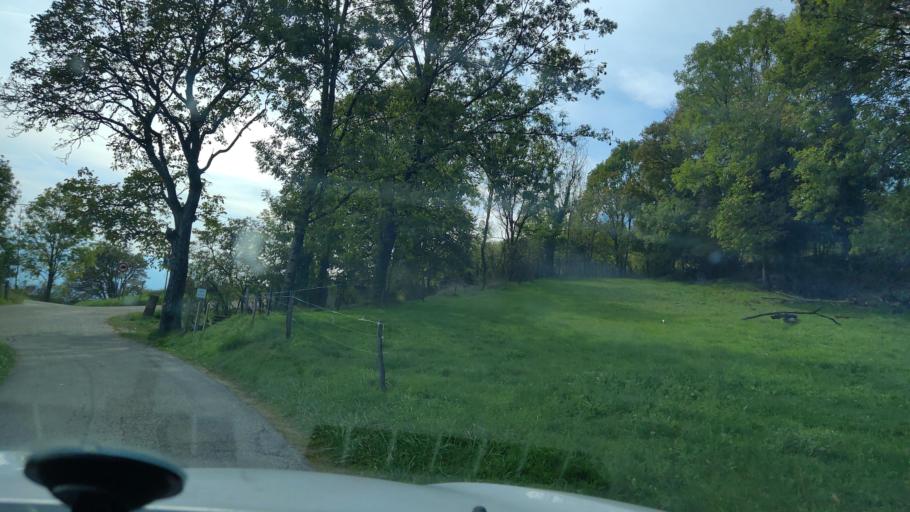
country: FR
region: Rhone-Alpes
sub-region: Departement de la Savoie
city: Coise-Saint-Jean-Pied-Gauthier
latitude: 45.5723
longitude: 6.1384
